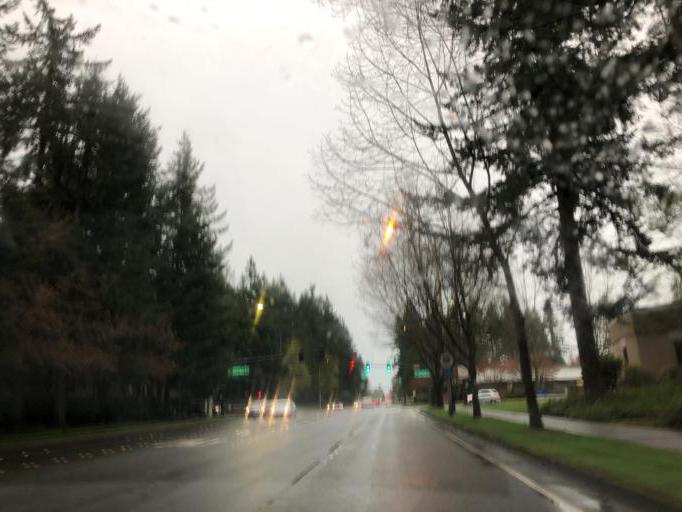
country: US
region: Washington
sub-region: Thurston County
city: Lacey
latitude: 47.0442
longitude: -122.8234
